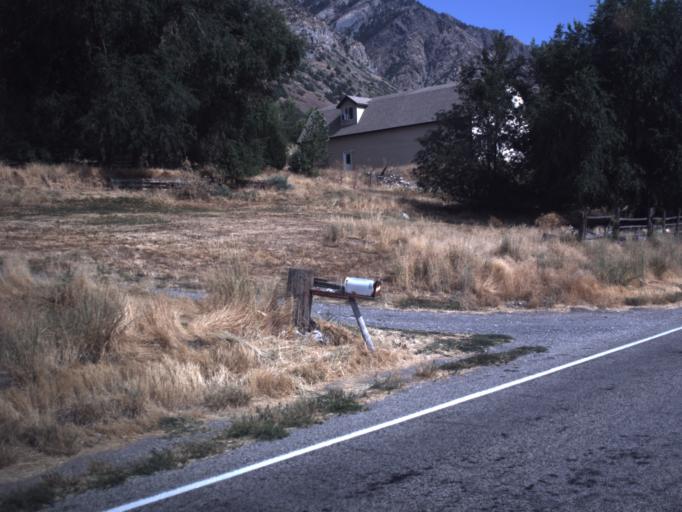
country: US
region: Utah
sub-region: Box Elder County
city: Brigham City
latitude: 41.5735
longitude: -112.0307
